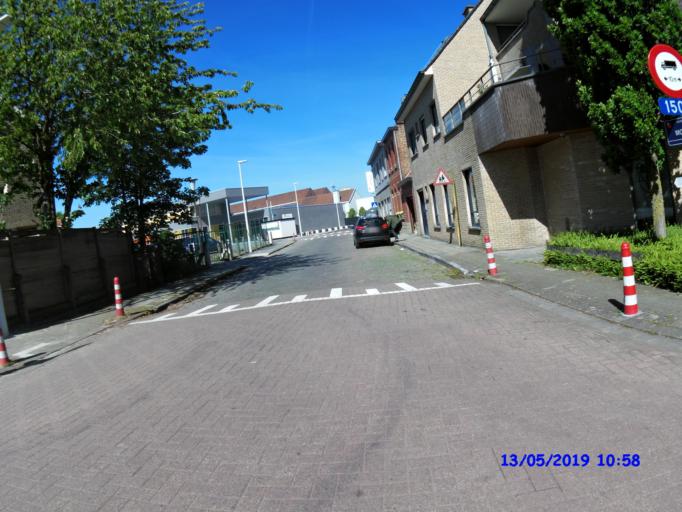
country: BE
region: Flanders
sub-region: Provincie West-Vlaanderen
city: Waregem
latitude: 50.8871
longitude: 3.4271
